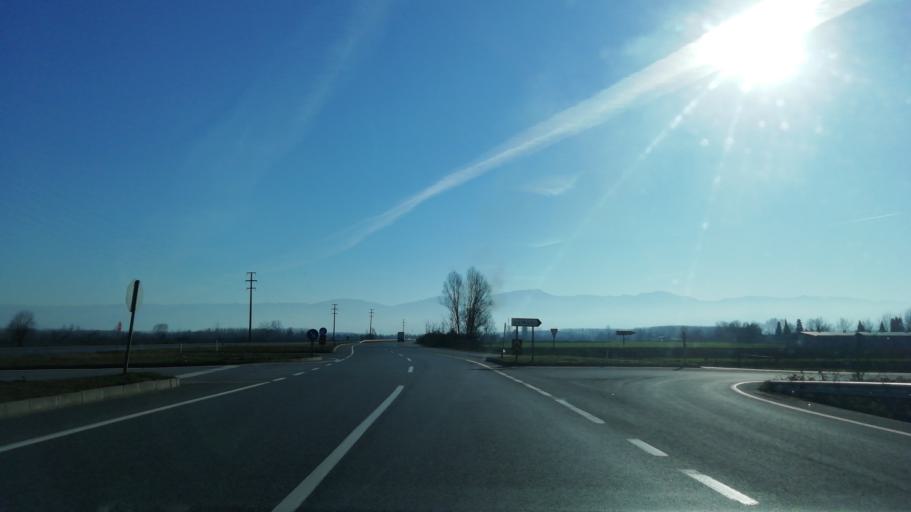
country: TR
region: Sakarya
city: Akyazi
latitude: 40.7348
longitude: 30.5652
